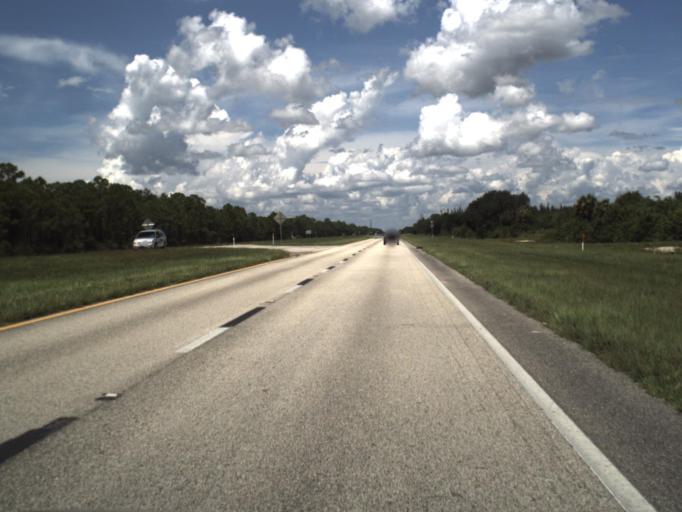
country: US
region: Florida
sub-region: Lee County
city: Burnt Store Marina
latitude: 26.8013
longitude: -81.9512
